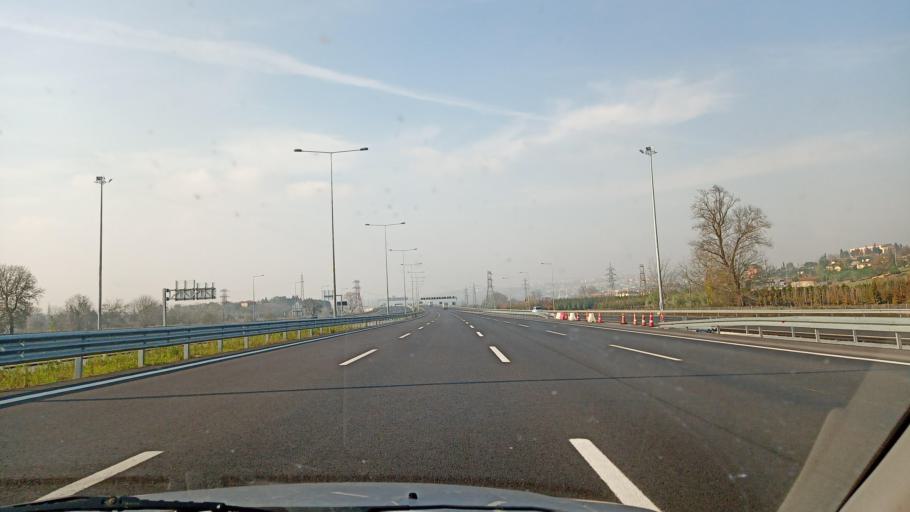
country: TR
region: Sakarya
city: Kazimpasa
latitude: 40.8430
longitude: 30.3423
